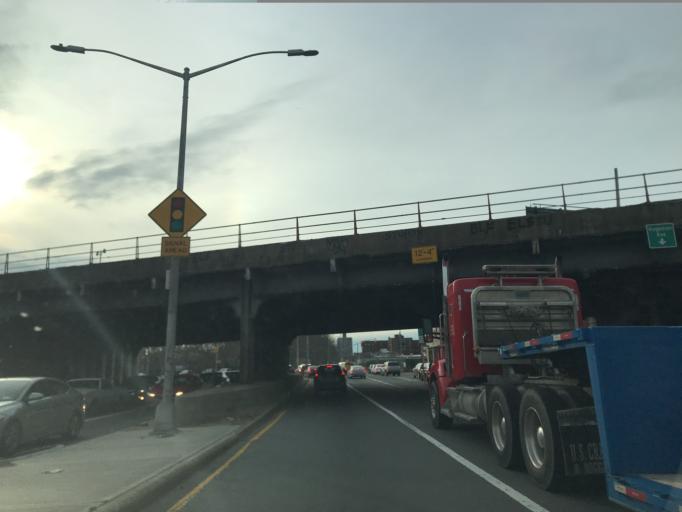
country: US
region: New York
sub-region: Kings County
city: East New York
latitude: 40.6574
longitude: -73.8993
